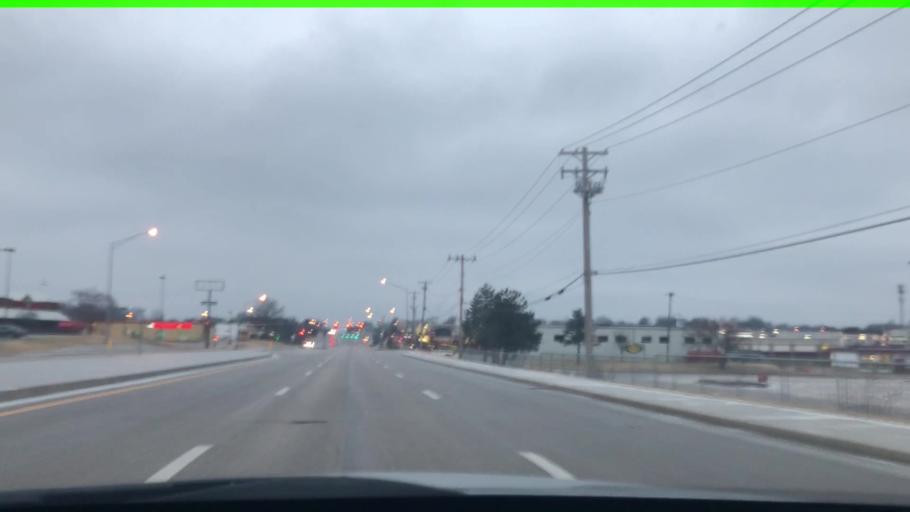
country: US
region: Missouri
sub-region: Boone County
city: Columbia
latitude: 38.9630
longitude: -92.3714
